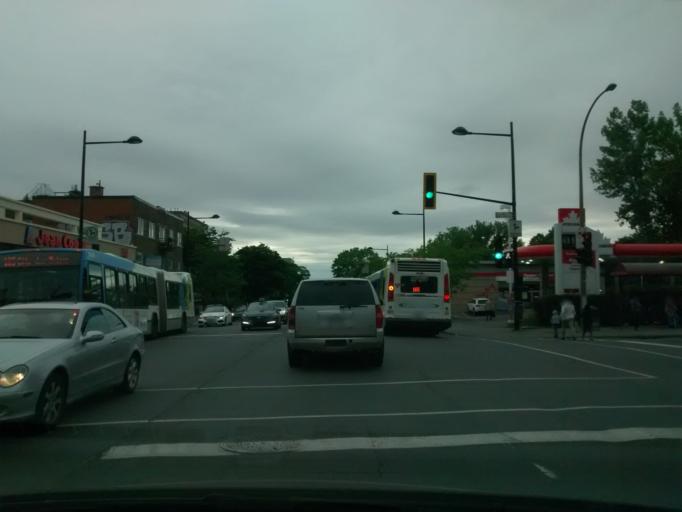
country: CA
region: Quebec
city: Mont-Royal
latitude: 45.5008
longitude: -73.6320
